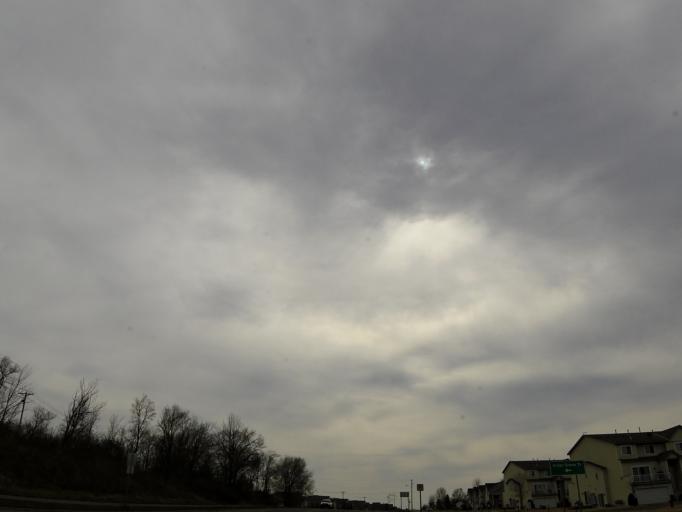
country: US
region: Minnesota
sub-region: Dakota County
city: Inver Grove Heights
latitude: 44.8317
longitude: -93.0232
